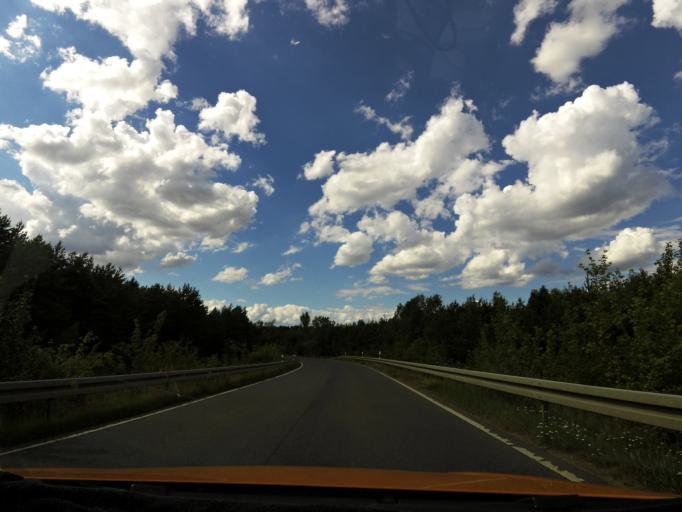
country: DE
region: Brandenburg
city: Wildau
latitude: 52.3089
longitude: 13.6725
